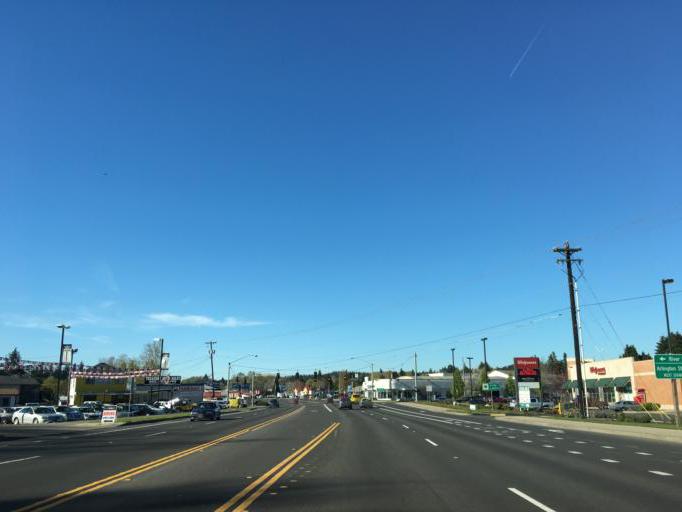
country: US
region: Oregon
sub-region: Clackamas County
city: Gladstone
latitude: 45.3743
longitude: -122.6016
